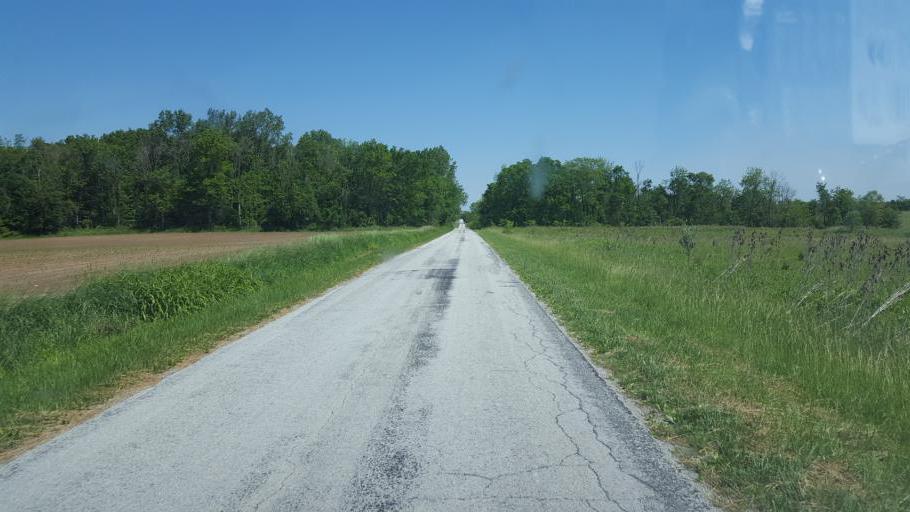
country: US
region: Ohio
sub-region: Hardin County
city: Kenton
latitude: 40.6353
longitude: -83.4387
